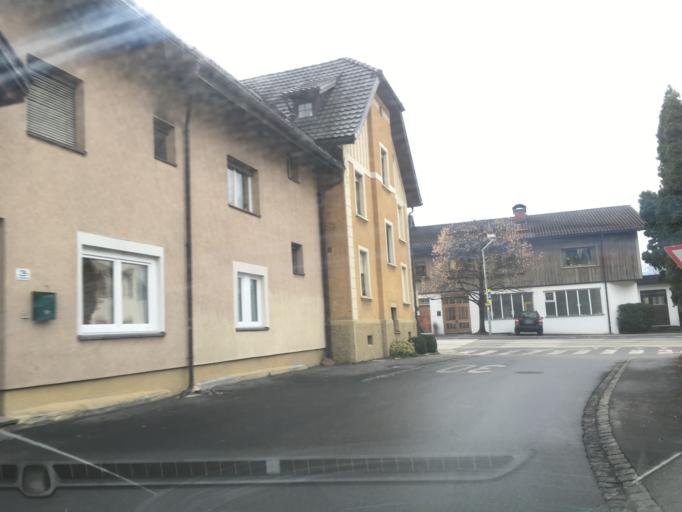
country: AT
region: Vorarlberg
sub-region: Politischer Bezirk Feldkirch
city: Rothis
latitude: 47.2936
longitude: 9.6519
